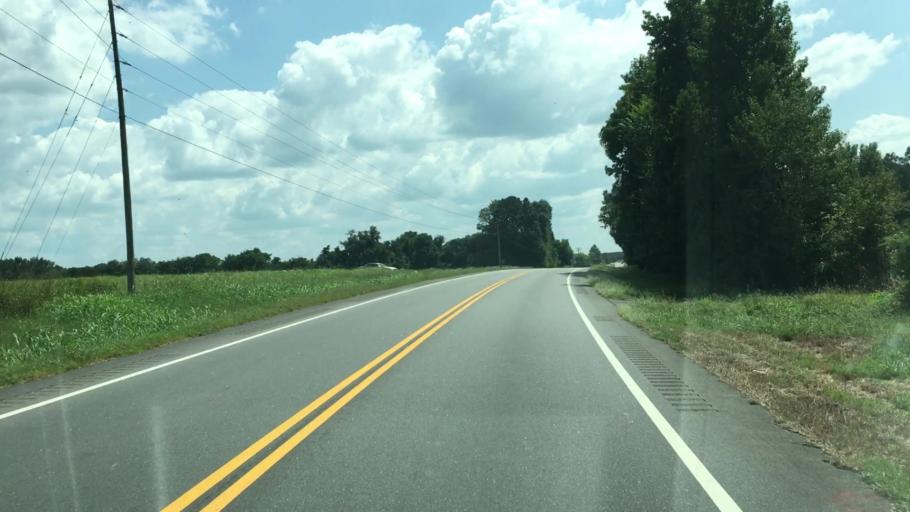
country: US
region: Georgia
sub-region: Morgan County
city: Madison
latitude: 33.5219
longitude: -83.4443
